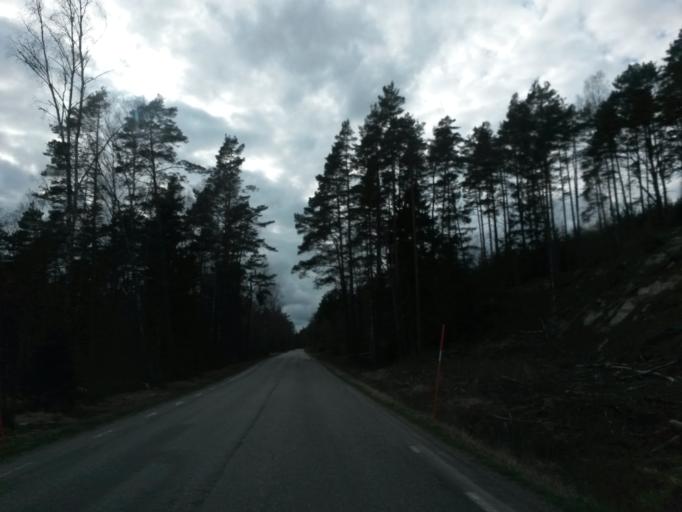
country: SE
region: Vaestra Goetaland
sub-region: Vargarda Kommun
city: Jonstorp
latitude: 57.9480
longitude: 12.6564
